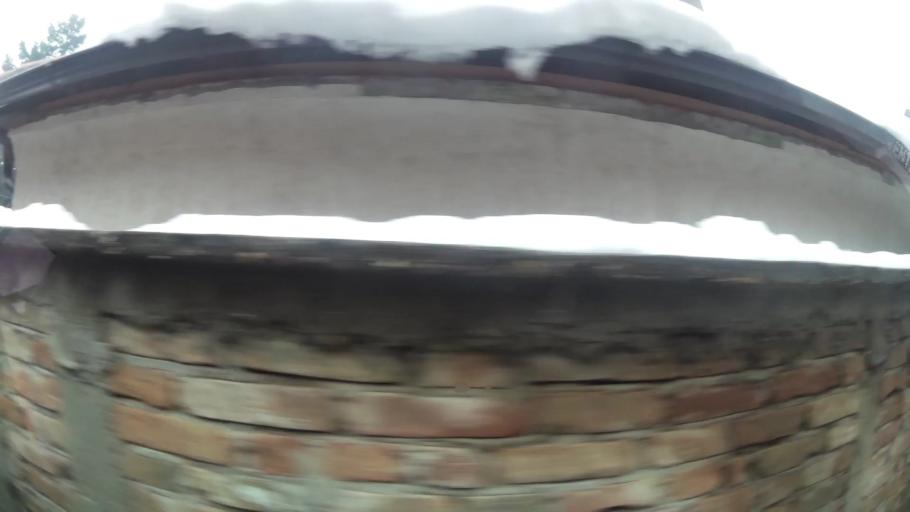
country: RS
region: Central Serbia
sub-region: Belgrade
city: Zvezdara
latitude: 44.7825
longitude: 20.5270
